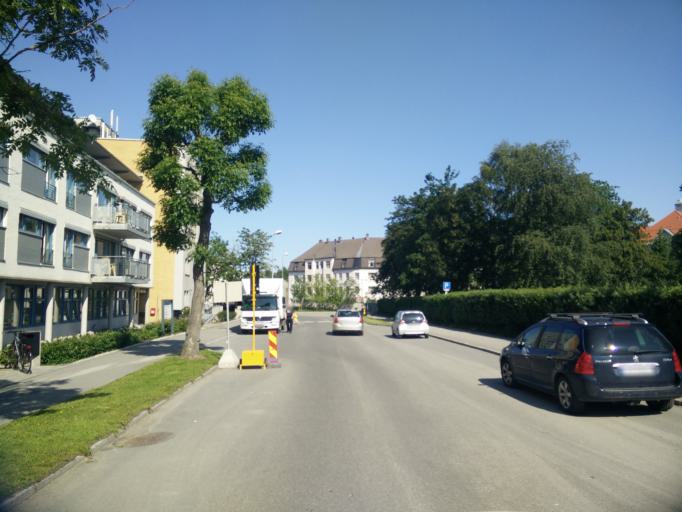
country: NO
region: Sor-Trondelag
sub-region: Trondheim
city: Trondheim
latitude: 63.4393
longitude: 10.4339
